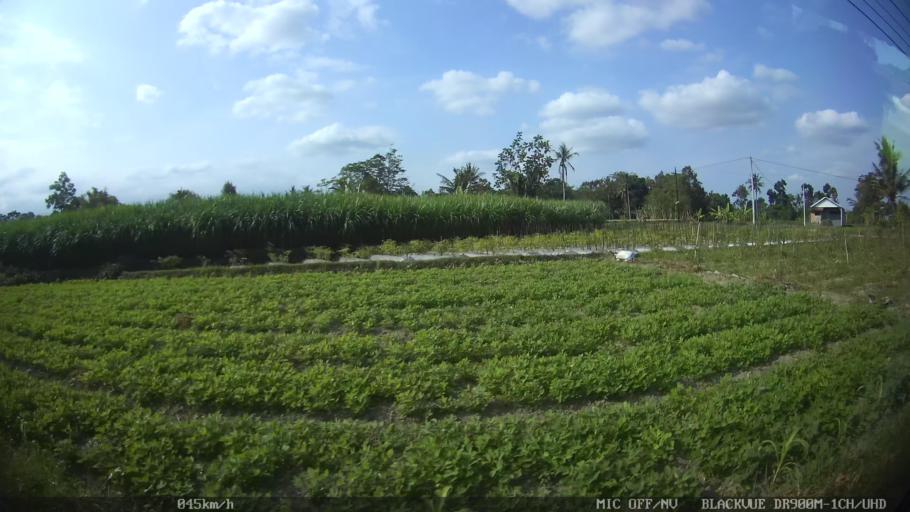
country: ID
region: Daerah Istimewa Yogyakarta
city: Depok
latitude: -7.7276
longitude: 110.4463
